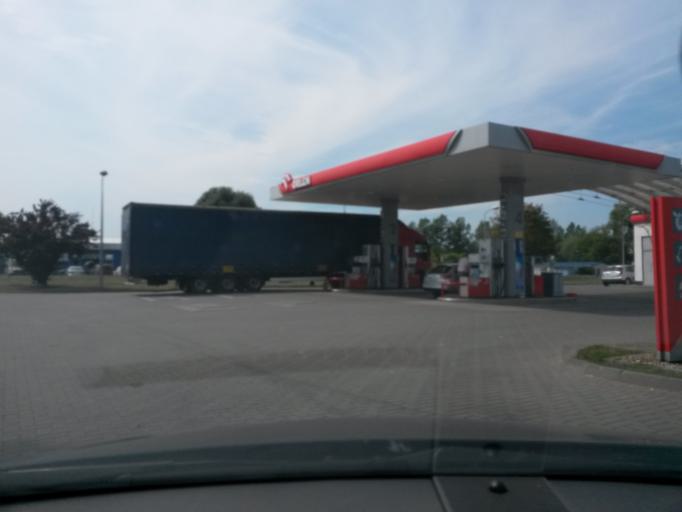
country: PL
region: Greater Poland Voivodeship
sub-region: Powiat sremski
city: Srem
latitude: 52.0681
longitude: 17.0378
